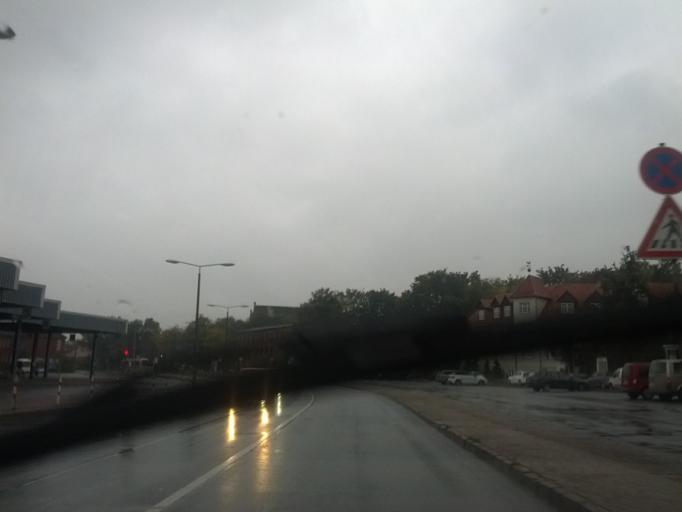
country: DE
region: Thuringia
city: Gotha
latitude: 50.9510
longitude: 10.7099
